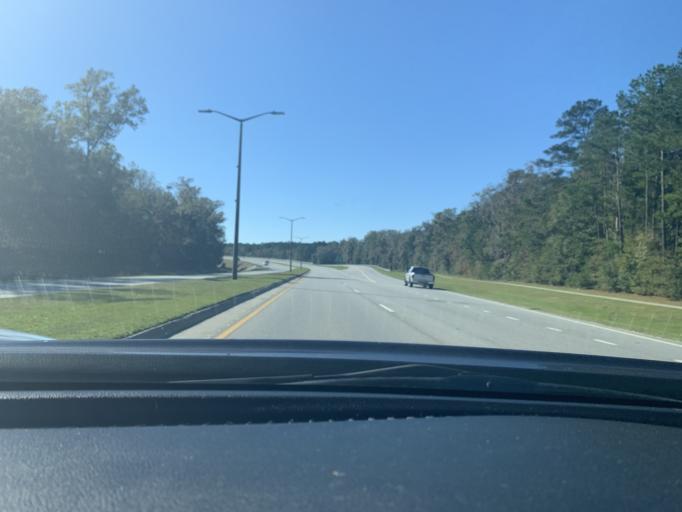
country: US
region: Georgia
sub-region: Chatham County
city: Pooler
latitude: 32.1264
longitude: -81.2635
